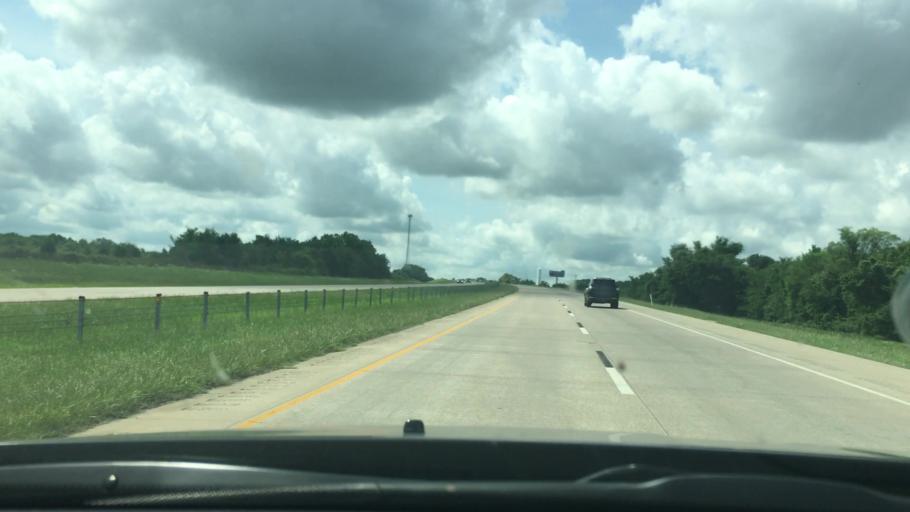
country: US
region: Oklahoma
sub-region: Love County
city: Marietta
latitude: 33.8452
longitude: -97.1341
